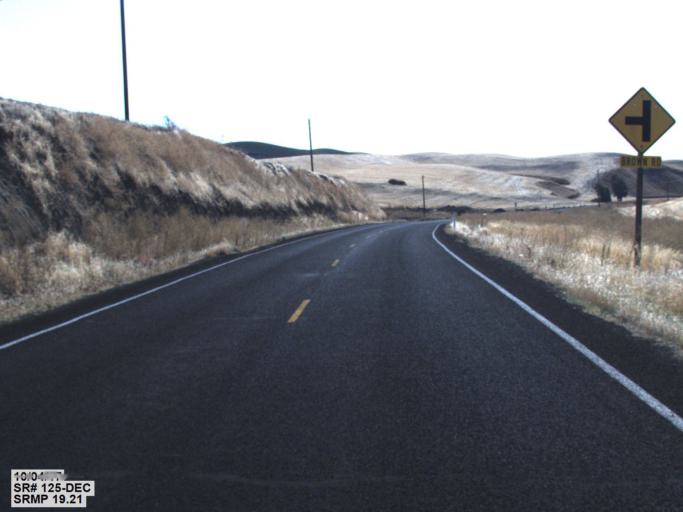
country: US
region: Washington
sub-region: Walla Walla County
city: Walla Walla
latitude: 46.2385
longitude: -118.3687
